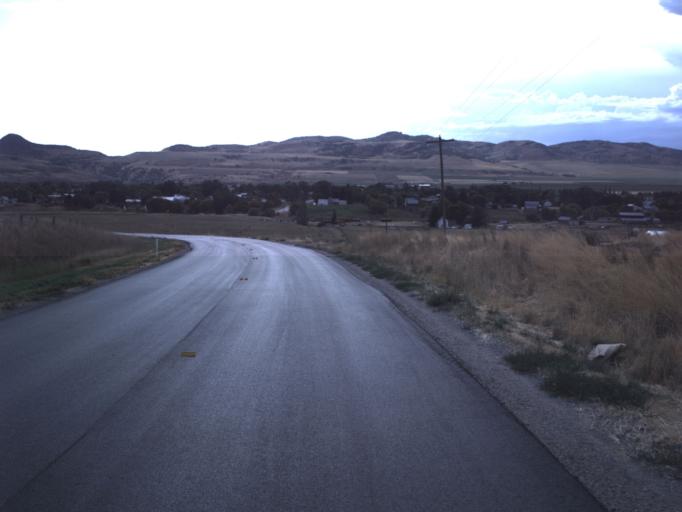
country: US
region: Utah
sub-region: Cache County
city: Benson
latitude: 41.8628
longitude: -111.9722
